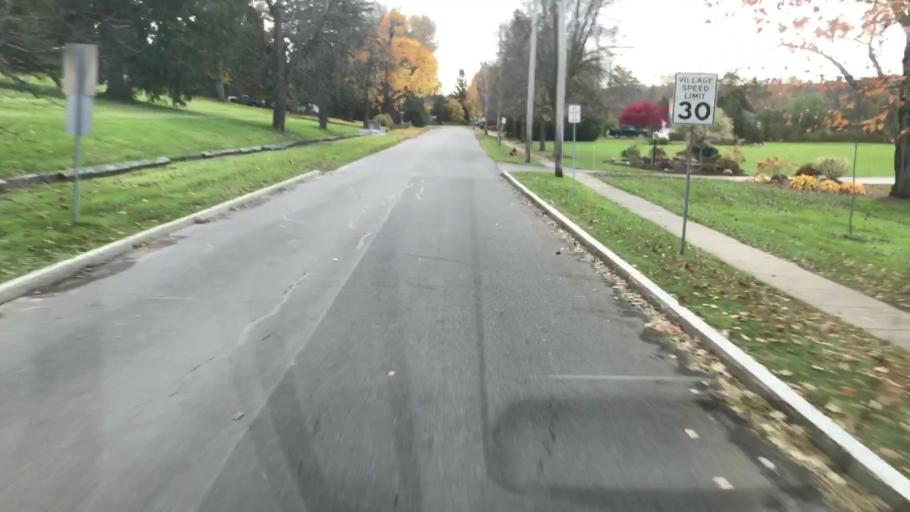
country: US
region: New York
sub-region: Onondaga County
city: Skaneateles
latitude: 42.9386
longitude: -76.4324
